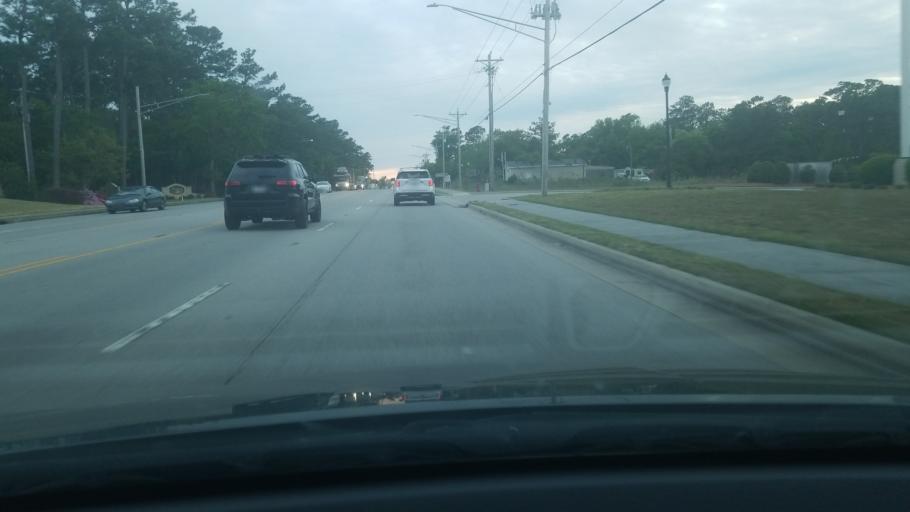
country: US
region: North Carolina
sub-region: Carteret County
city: Cedar Point
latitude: 34.6870
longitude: -77.0740
